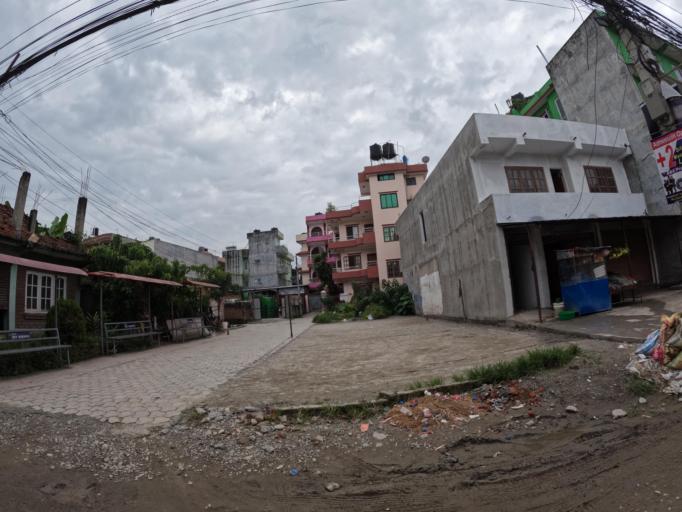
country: NP
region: Central Region
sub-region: Bagmati Zone
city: Kathmandu
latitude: 27.7451
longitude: 85.3193
